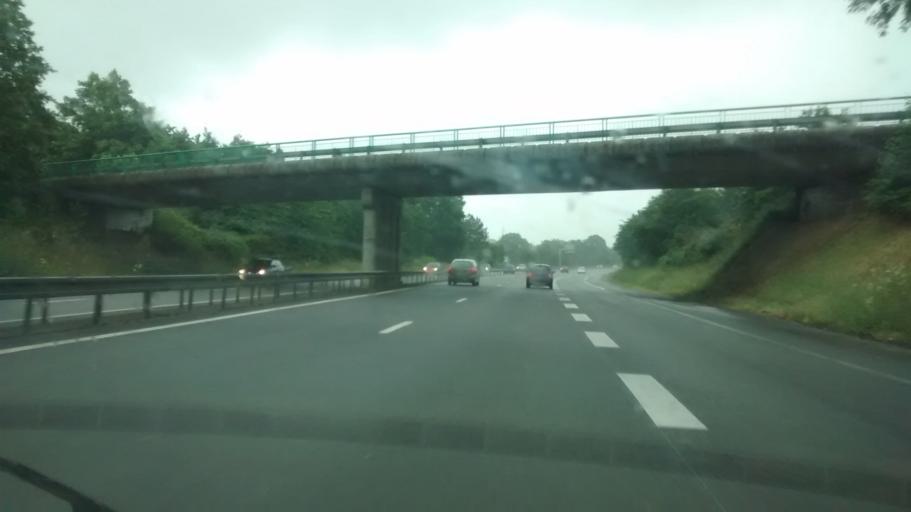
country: FR
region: Brittany
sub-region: Departement du Morbihan
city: Auray
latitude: 47.6829
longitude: -3.0237
